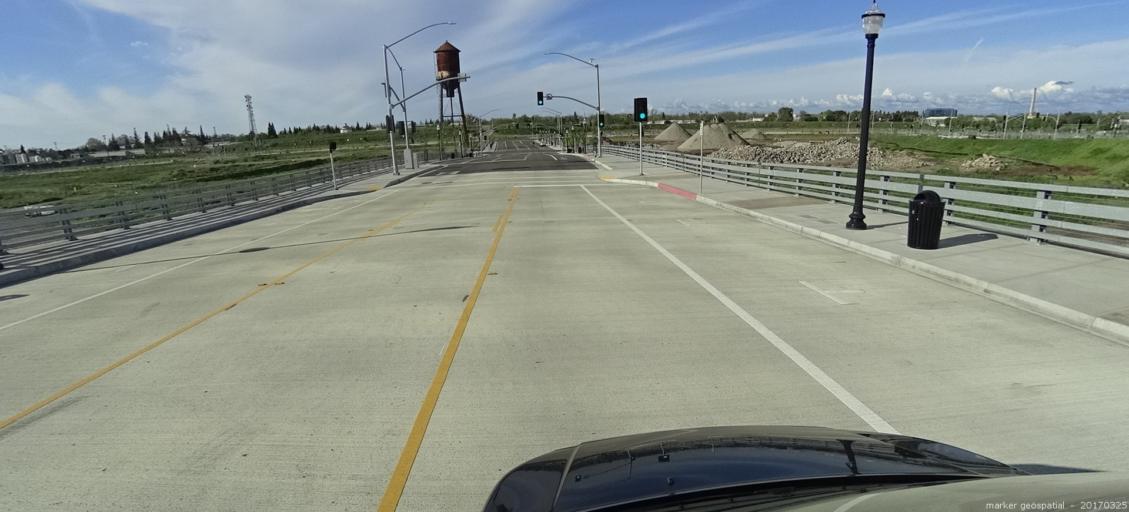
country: US
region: California
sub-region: Sacramento County
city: Sacramento
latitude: 38.5875
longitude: -121.4975
